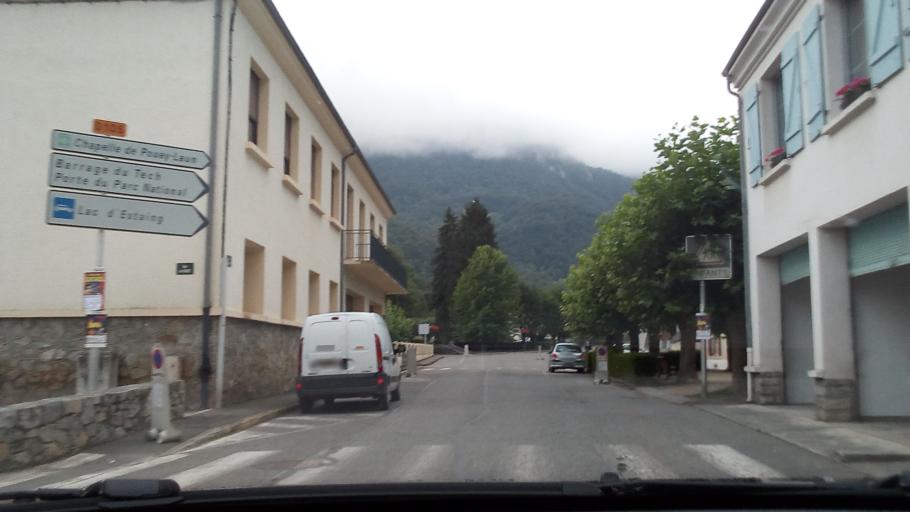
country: FR
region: Midi-Pyrenees
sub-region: Departement des Hautes-Pyrenees
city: Cauterets
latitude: 42.9555
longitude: -0.2138
